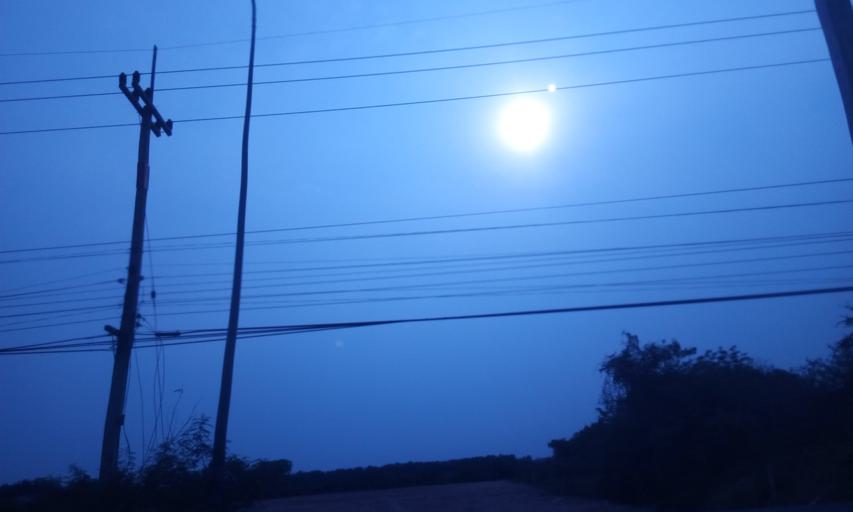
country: TH
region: Chachoengsao
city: Ban Pho
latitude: 13.6287
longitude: 101.1057
